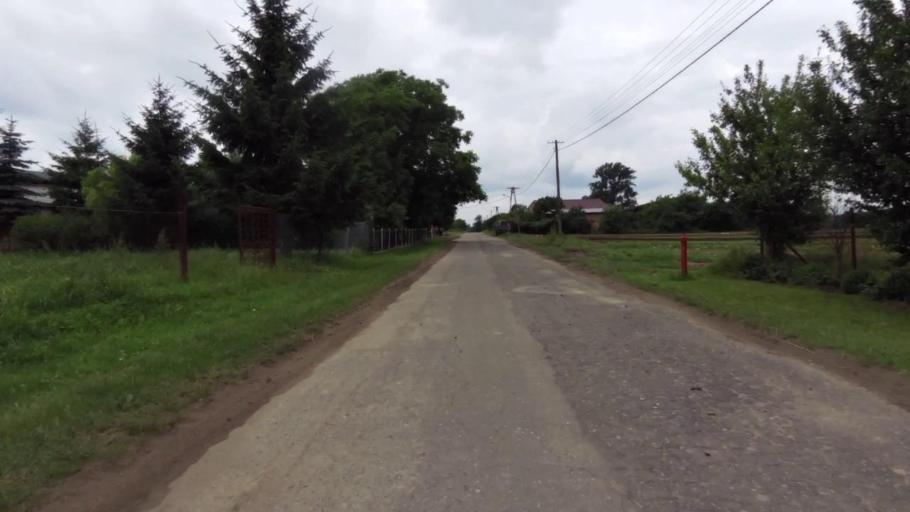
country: PL
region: West Pomeranian Voivodeship
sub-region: Powiat pyrzycki
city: Lipiany
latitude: 52.9644
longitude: 14.9563
